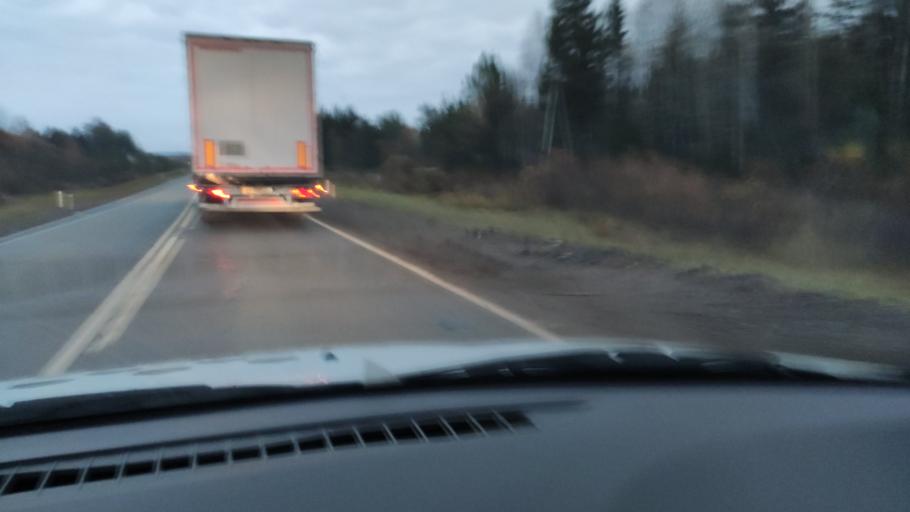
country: RU
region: Kirov
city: Kostino
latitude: 58.8549
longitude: 53.2022
